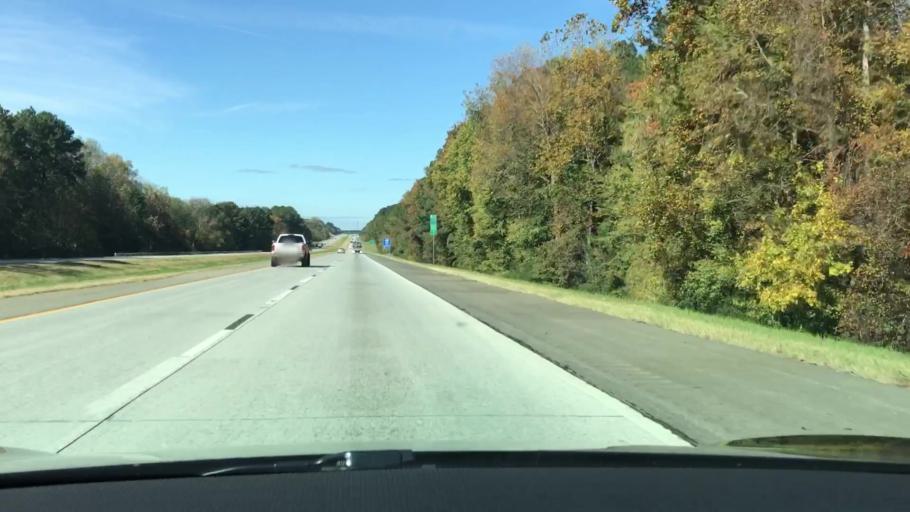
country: US
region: Georgia
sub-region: Putnam County
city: Jefferson
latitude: 33.5457
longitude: -83.3358
